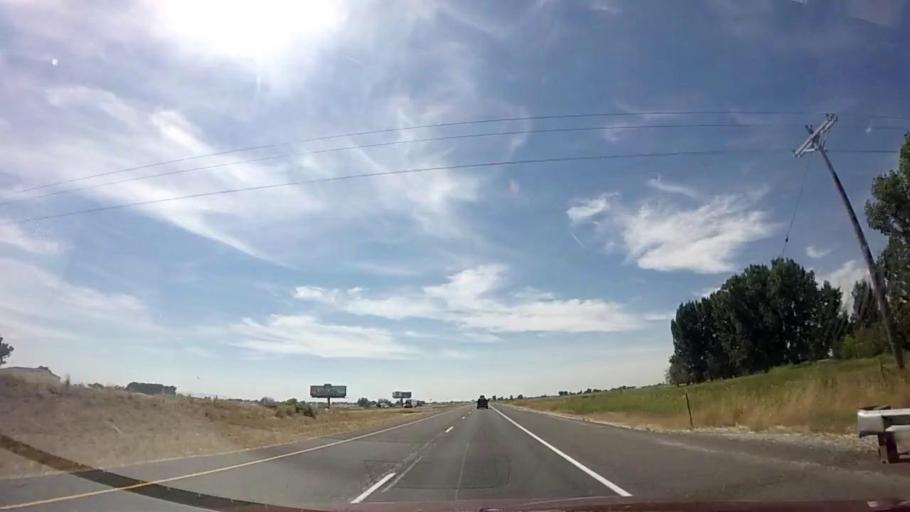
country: US
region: Idaho
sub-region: Minidoka County
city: Rupert
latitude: 42.5691
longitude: -113.7058
